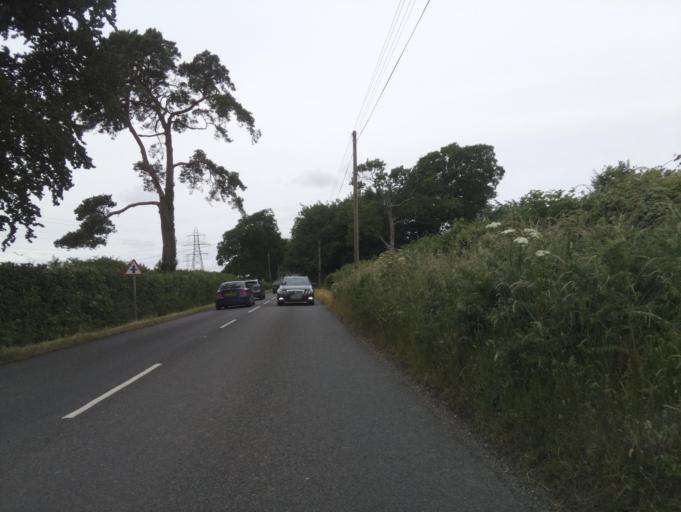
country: GB
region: England
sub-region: Devon
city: Ottery St Mary
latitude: 50.7502
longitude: -3.3151
